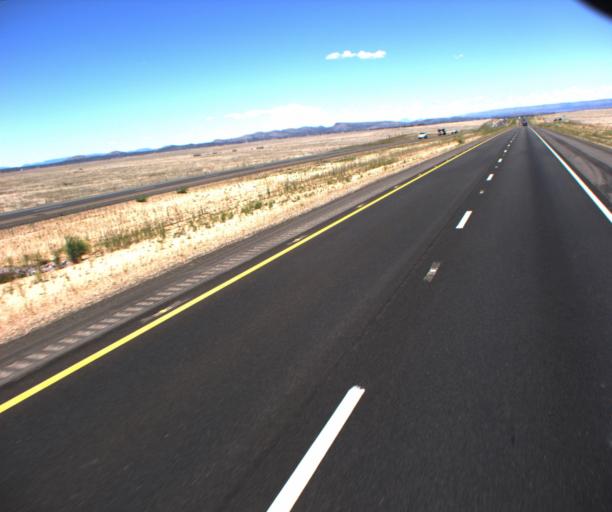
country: US
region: Arizona
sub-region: Yavapai County
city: Chino Valley
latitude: 34.6845
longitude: -112.4443
